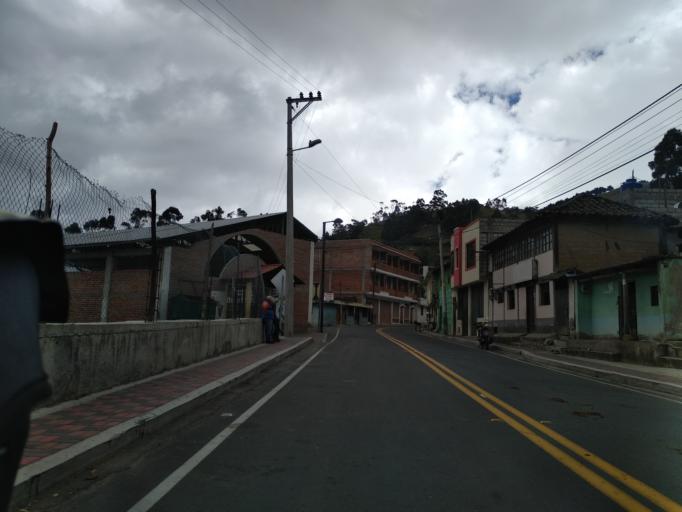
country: EC
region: Cotopaxi
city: Saquisili
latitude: -0.7993
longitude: -78.9197
